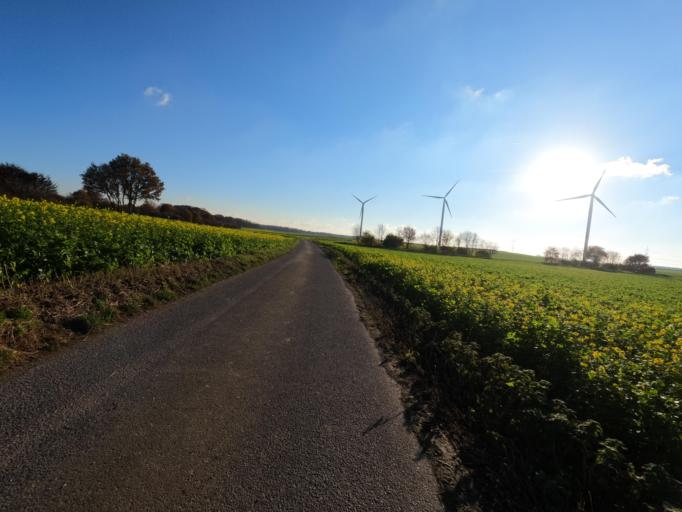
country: DE
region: North Rhine-Westphalia
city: Geilenkirchen
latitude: 51.0127
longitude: 6.1366
